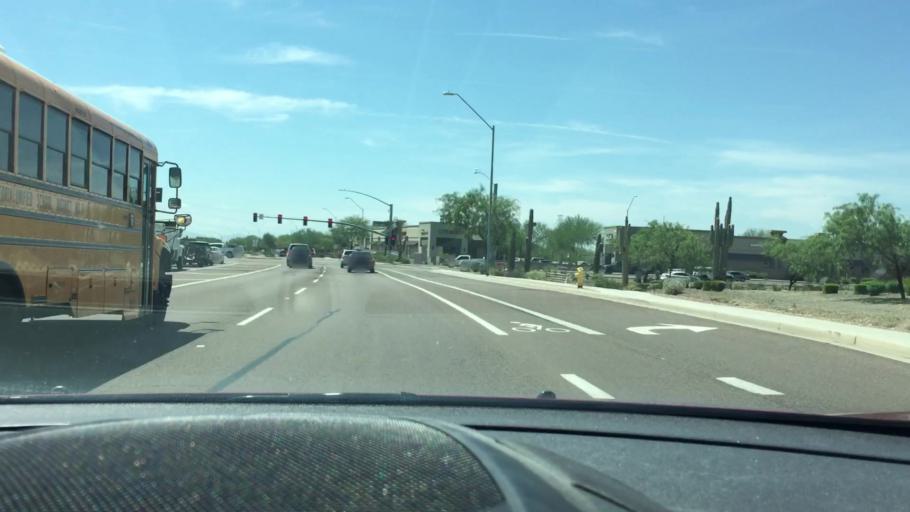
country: US
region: Arizona
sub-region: Maricopa County
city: Sun City West
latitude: 33.7121
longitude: -112.2728
